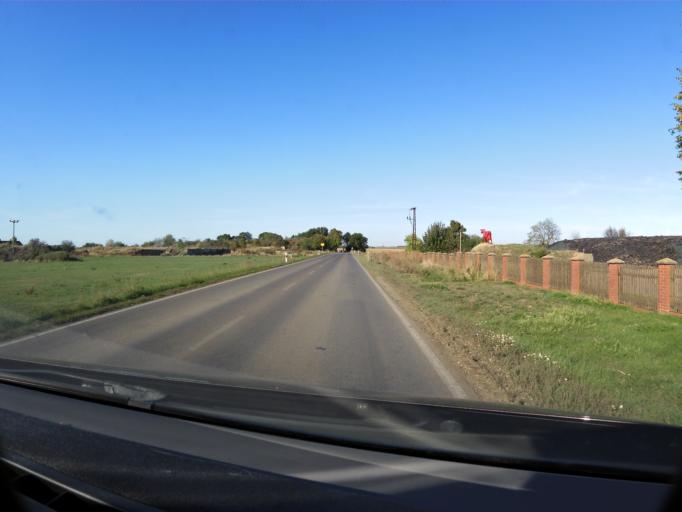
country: DE
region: Saxony-Anhalt
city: Wegeleben
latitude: 51.8960
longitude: 11.1879
